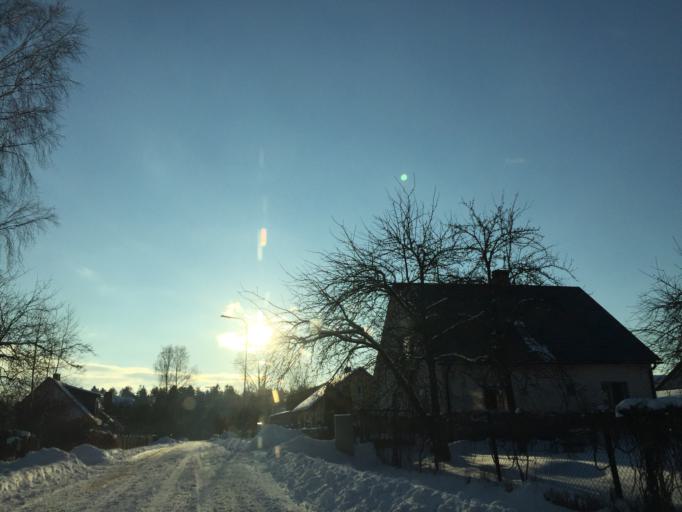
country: LV
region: Incukalns
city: Incukalns
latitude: 57.1058
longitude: 24.6782
